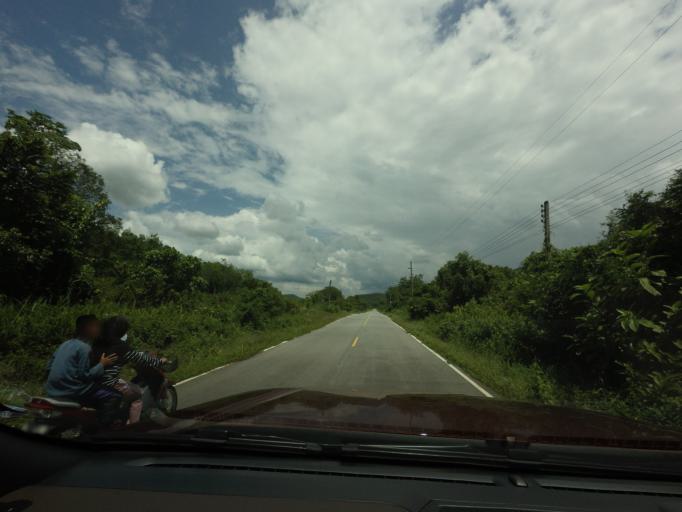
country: TH
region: Narathiwat
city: Chanae
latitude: 6.0628
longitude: 101.6877
